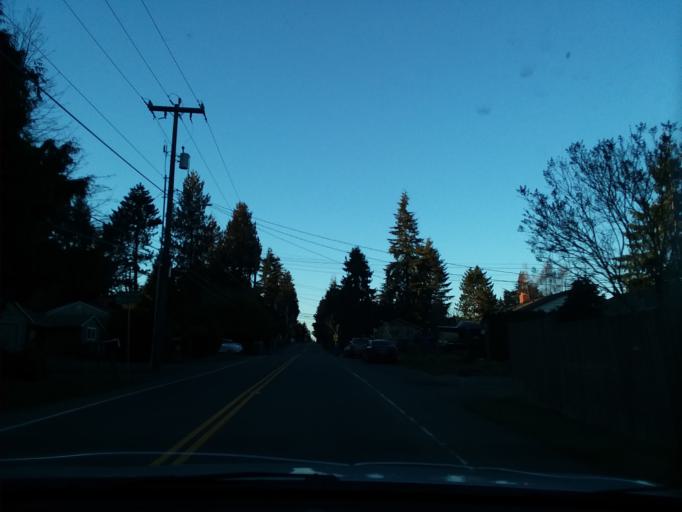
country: US
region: Washington
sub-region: Snohomish County
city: Mountlake Terrace
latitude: 47.7730
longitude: -122.2975
